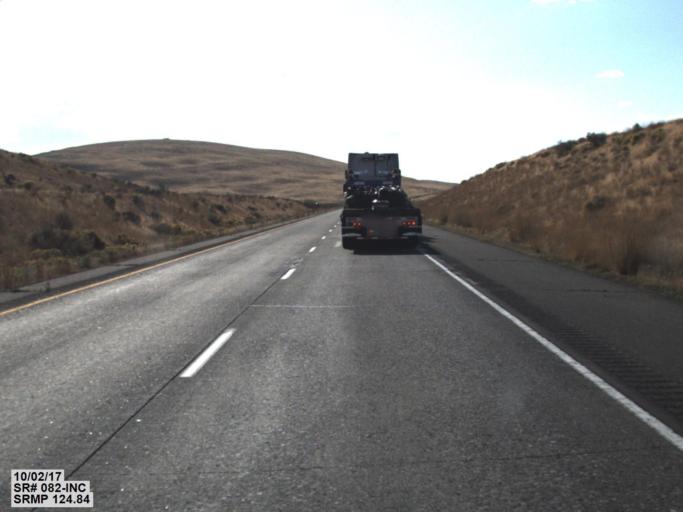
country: US
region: Oregon
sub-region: Umatilla County
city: Umatilla
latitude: 46.0032
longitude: -119.2510
